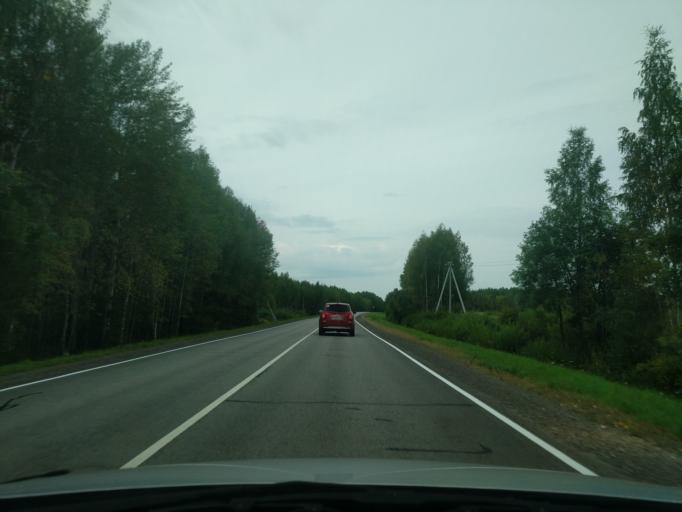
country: RU
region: Kirov
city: Kotel'nich
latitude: 58.2711
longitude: 48.1011
